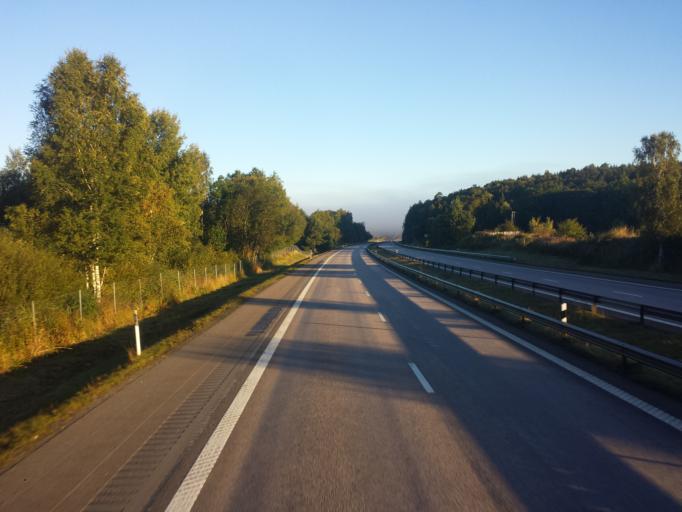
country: SE
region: Halland
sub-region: Kungsbacka Kommun
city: Fjaeras kyrkby
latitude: 57.4097
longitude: 12.1737
